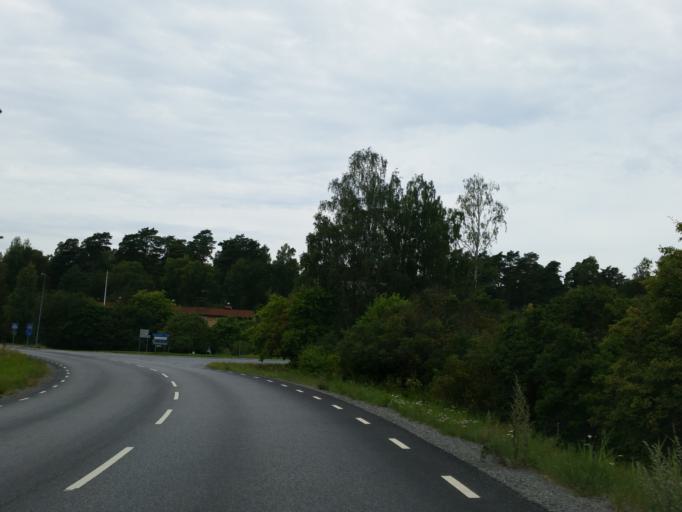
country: SE
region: Stockholm
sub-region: Botkyrka Kommun
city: Eriksberg
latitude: 59.2420
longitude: 17.7874
